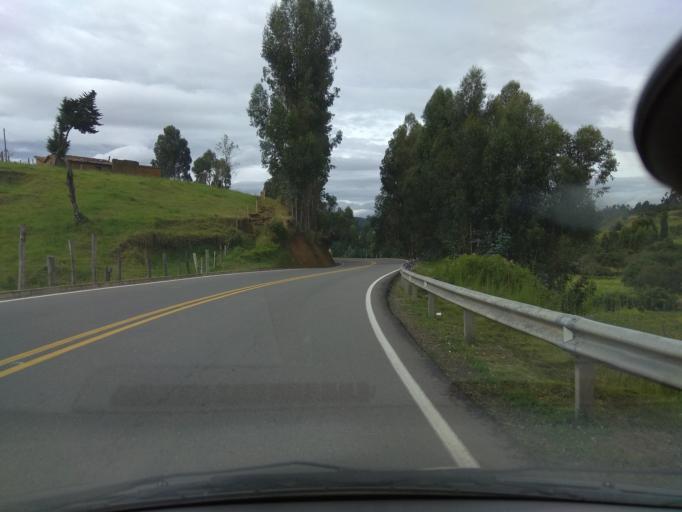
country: CO
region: Boyaca
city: Santa Rosa de Viterbo
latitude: 5.8978
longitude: -72.9758
